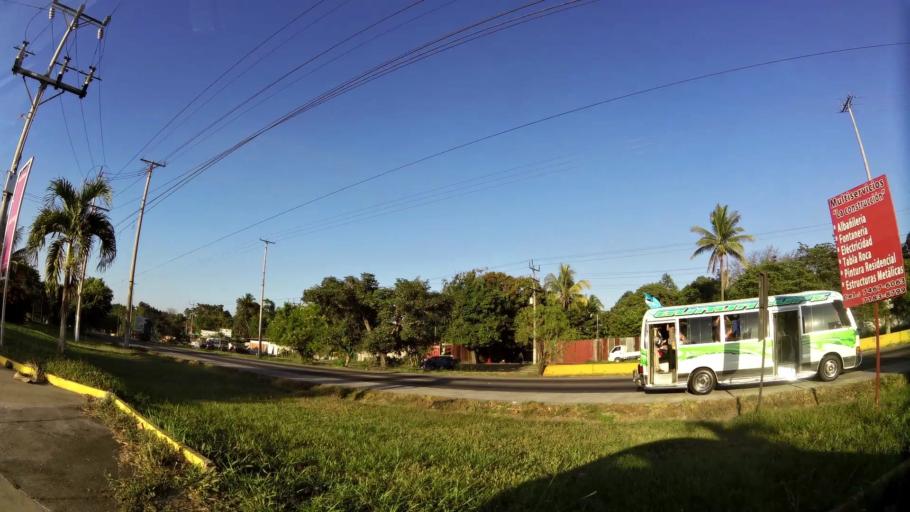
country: SV
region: La Libertad
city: Santa Tecla
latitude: 13.7551
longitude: -89.3668
